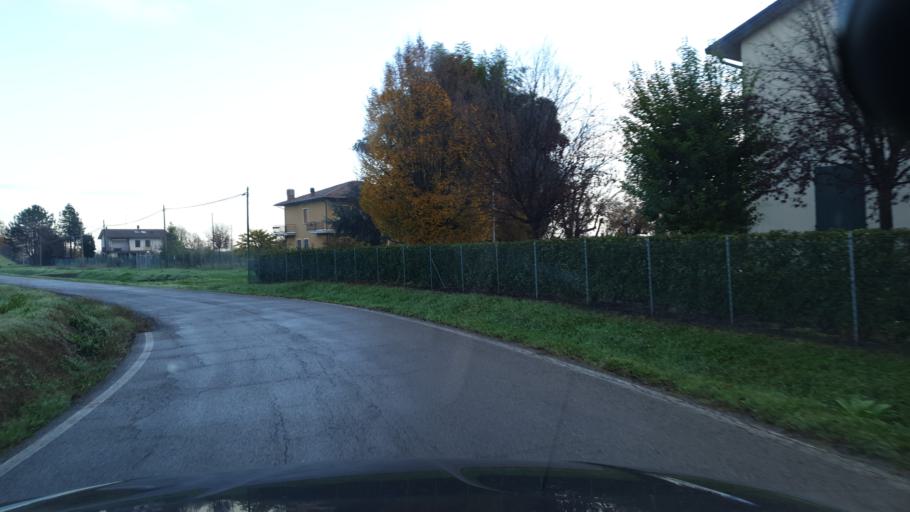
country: IT
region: Emilia-Romagna
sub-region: Provincia di Bologna
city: Crespellano
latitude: 44.5219
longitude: 11.1465
